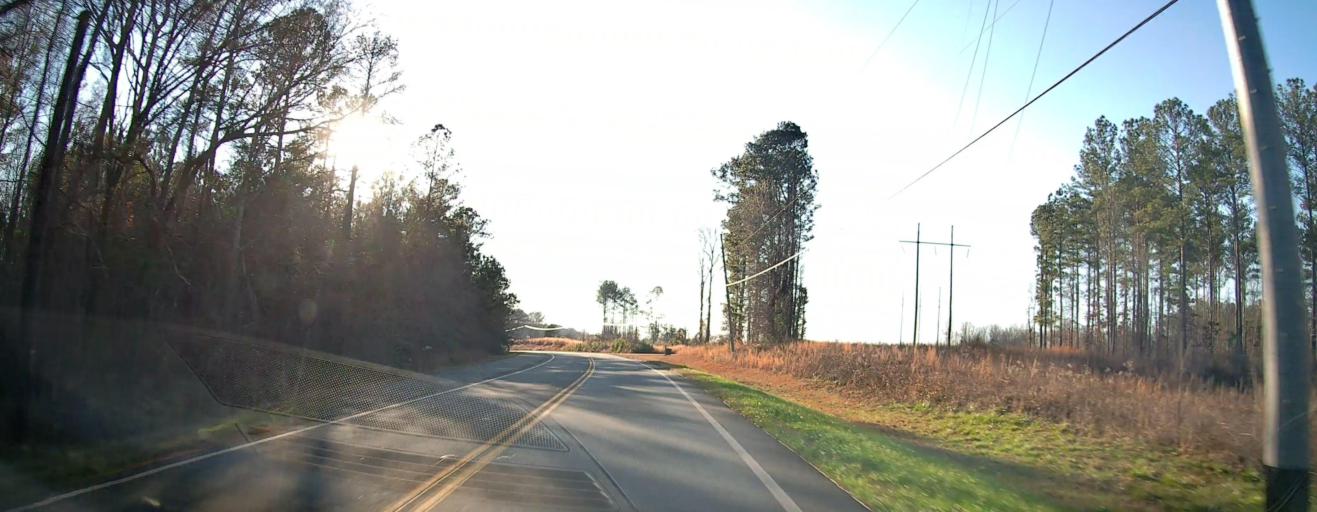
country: US
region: Georgia
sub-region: Harris County
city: Pine Mountain
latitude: 32.9162
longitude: -84.7952
